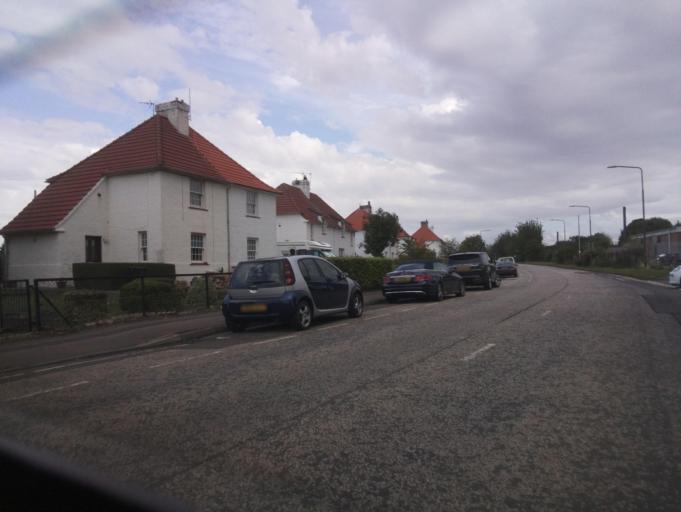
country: GB
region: Scotland
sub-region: East Lothian
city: Prestonpans
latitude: 55.9536
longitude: -2.9740
